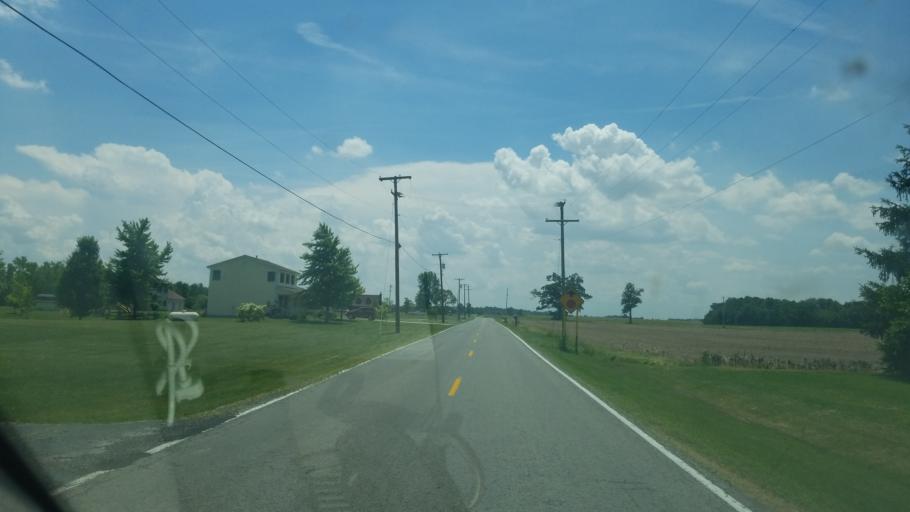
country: US
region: Ohio
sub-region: Hancock County
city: Arlington
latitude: 40.9090
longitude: -83.5947
